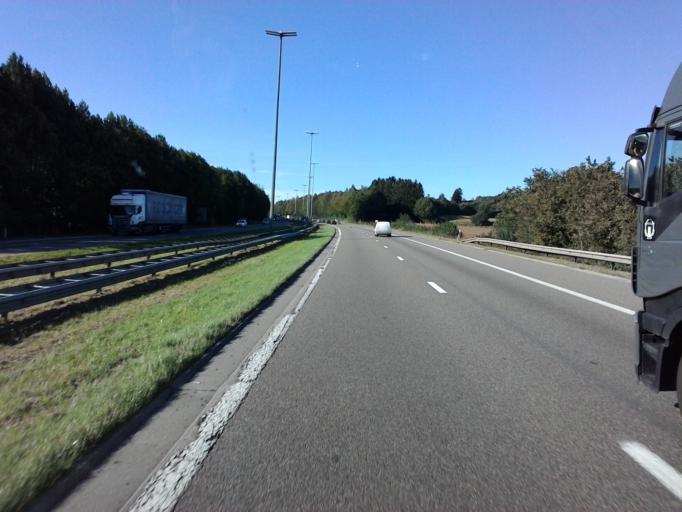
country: BE
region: Wallonia
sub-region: Province du Luxembourg
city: Arlon
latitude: 49.6582
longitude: 5.8154
